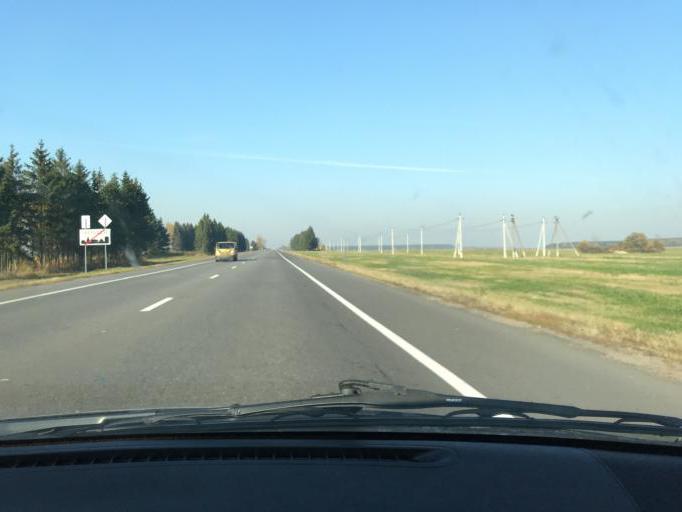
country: BY
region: Mogilev
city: Shklow
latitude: 54.2615
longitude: 30.4502
